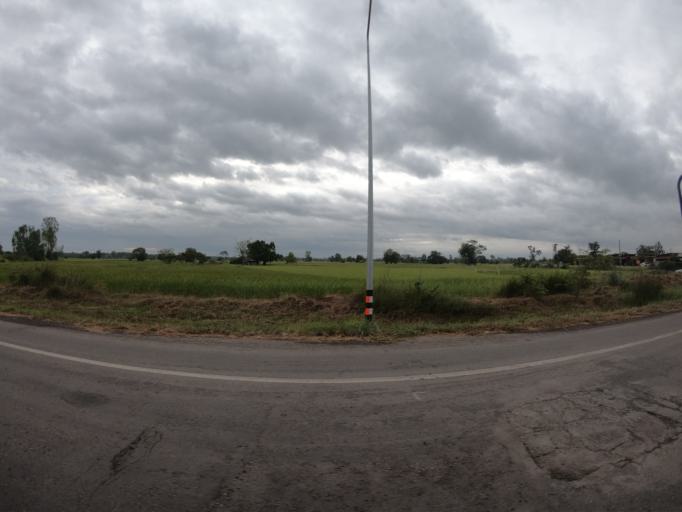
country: TH
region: Roi Et
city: Chiang Khwan
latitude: 16.1371
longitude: 103.8553
